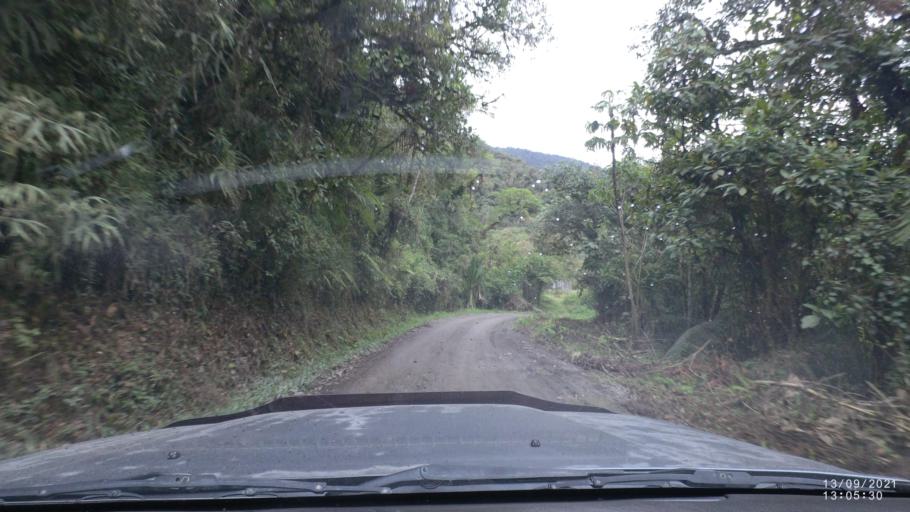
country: BO
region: Cochabamba
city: Colomi
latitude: -17.2233
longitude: -65.8229
